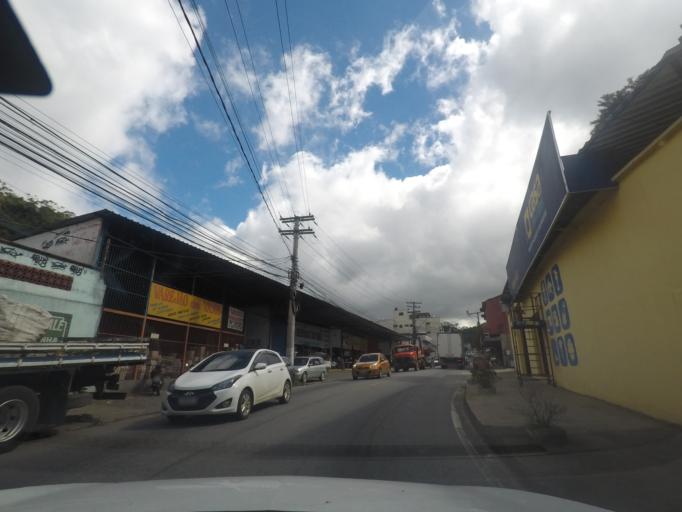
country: BR
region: Rio de Janeiro
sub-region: Teresopolis
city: Teresopolis
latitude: -22.4019
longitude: -42.9641
